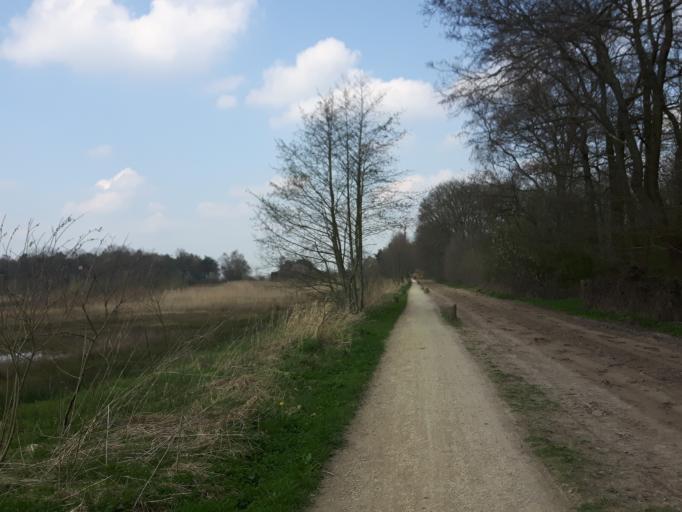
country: NL
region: Overijssel
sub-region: Gemeente Haaksbergen
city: Haaksbergen
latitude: 52.1577
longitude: 6.8131
